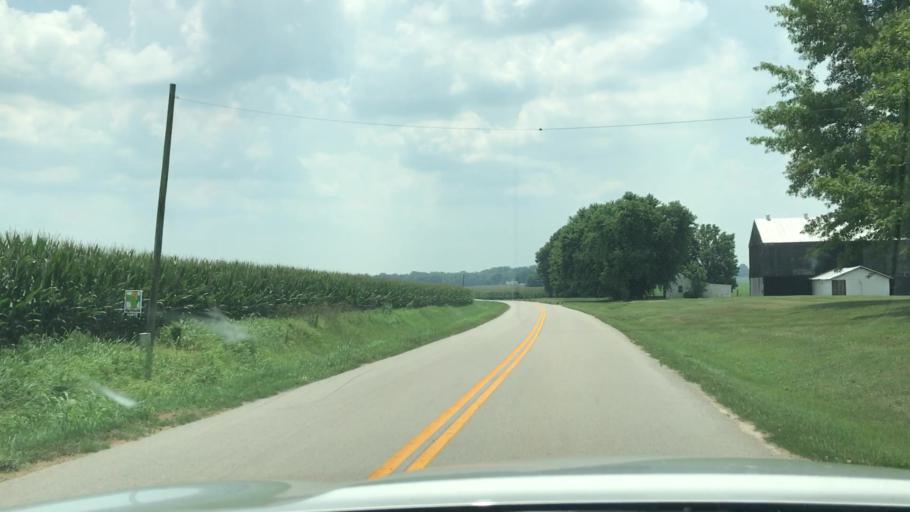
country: US
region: Kentucky
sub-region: Todd County
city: Elkton
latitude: 36.7546
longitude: -87.0966
